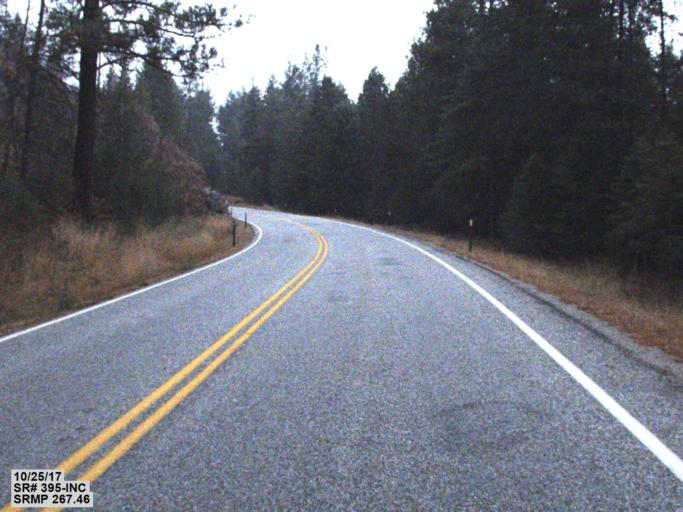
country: CA
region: British Columbia
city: Grand Forks
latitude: 48.9614
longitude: -118.2147
